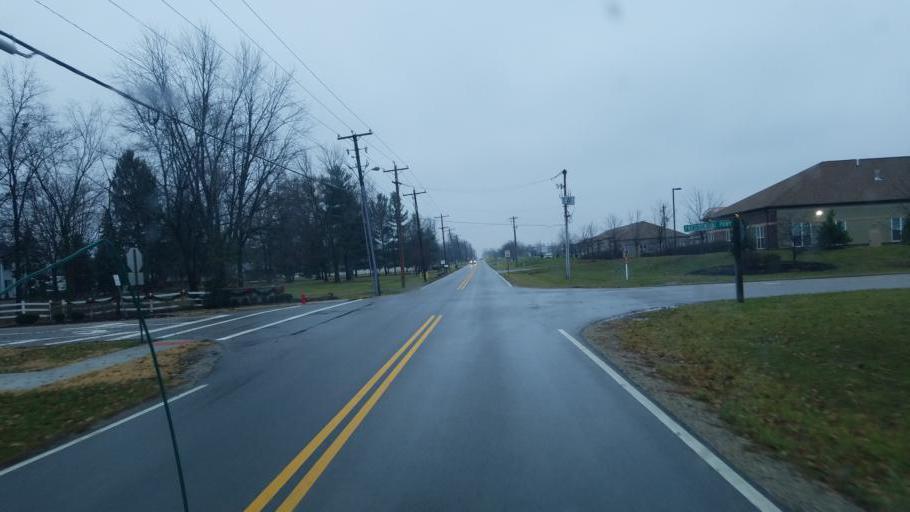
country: US
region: Ohio
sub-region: Delaware County
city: Powell
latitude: 40.1492
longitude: -83.0889
